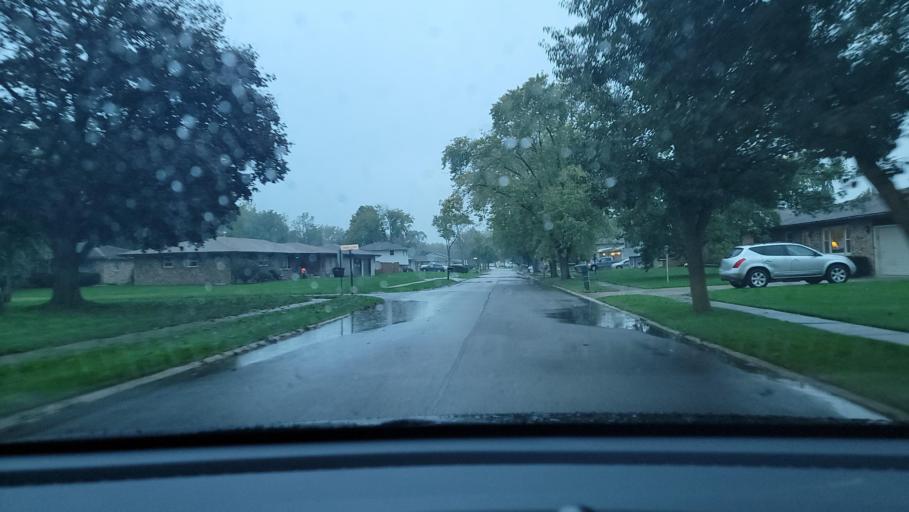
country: US
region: Indiana
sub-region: Porter County
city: Portage
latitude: 41.5681
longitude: -87.1921
